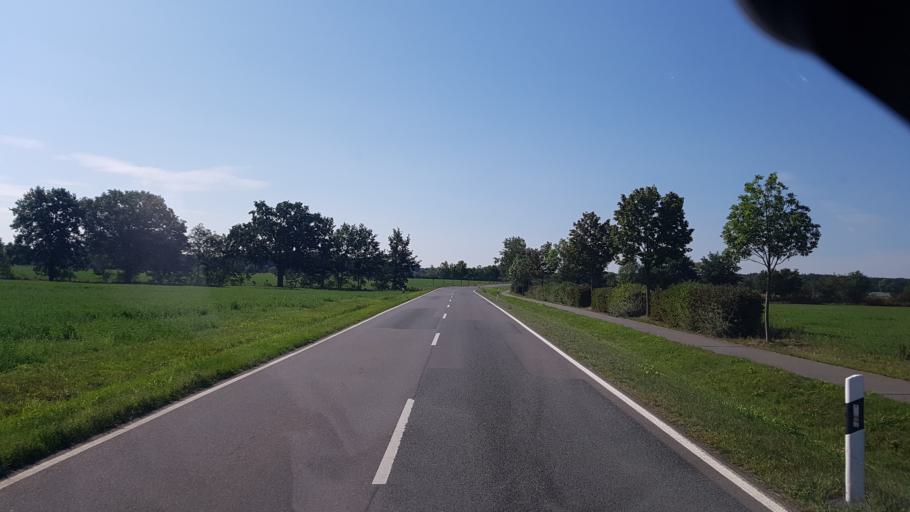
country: DE
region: Brandenburg
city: Vetschau
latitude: 51.7243
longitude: 14.0440
